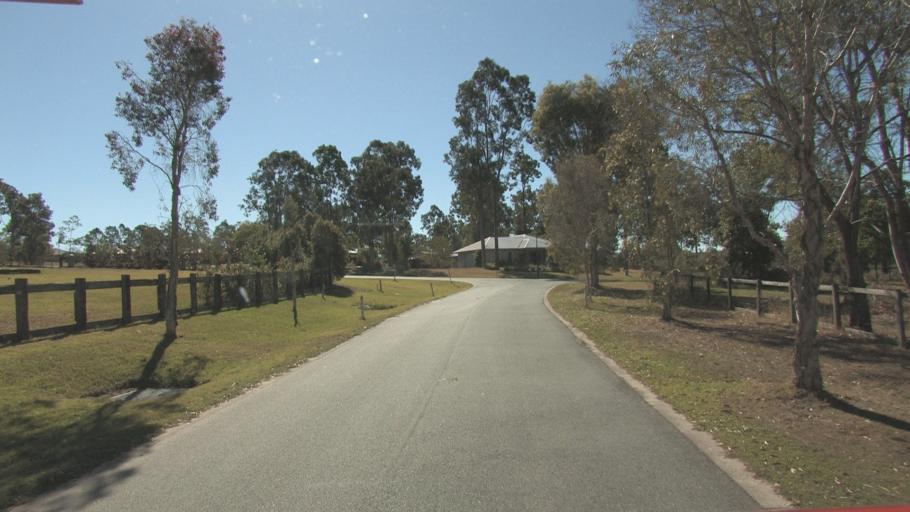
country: AU
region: Queensland
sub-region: Logan
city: North Maclean
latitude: -27.7583
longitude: 152.9583
